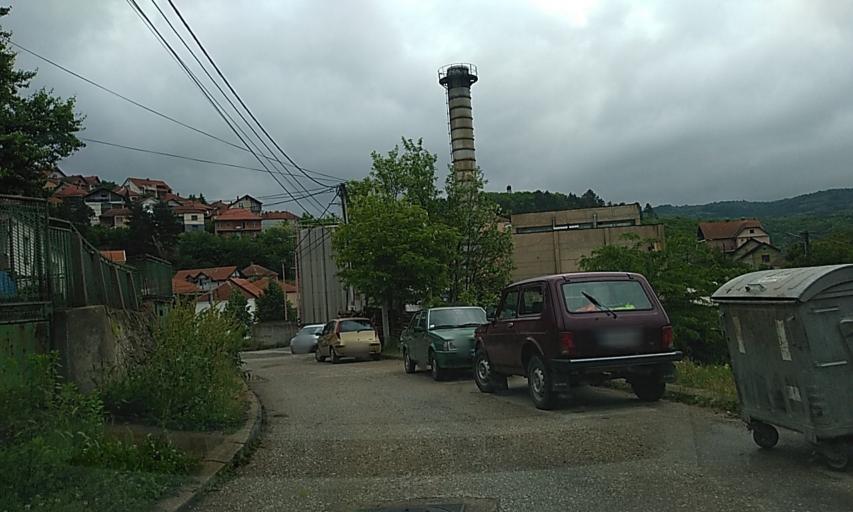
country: RS
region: Central Serbia
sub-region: Pcinjski Okrug
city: Vladicin Han
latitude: 42.7148
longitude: 22.0633
